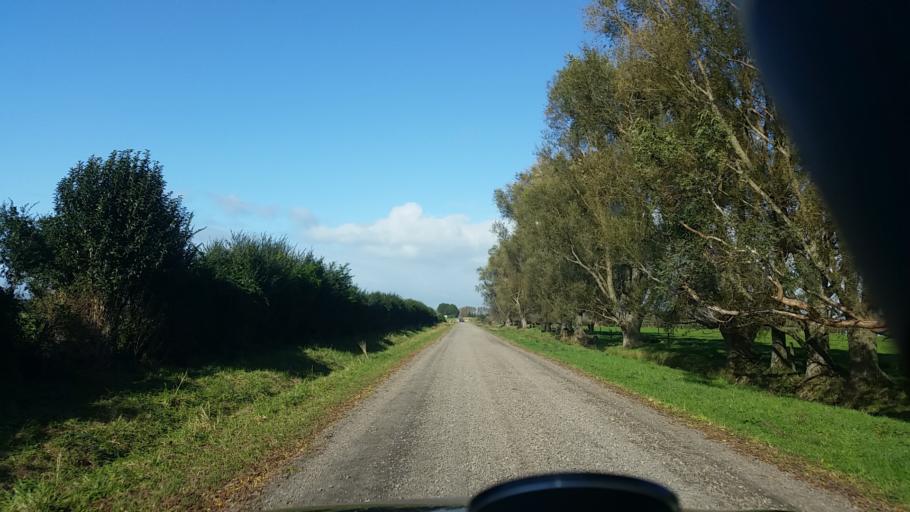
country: NZ
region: Bay of Plenty
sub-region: Western Bay of Plenty District
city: Katikati
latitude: -37.5887
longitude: 175.7132
